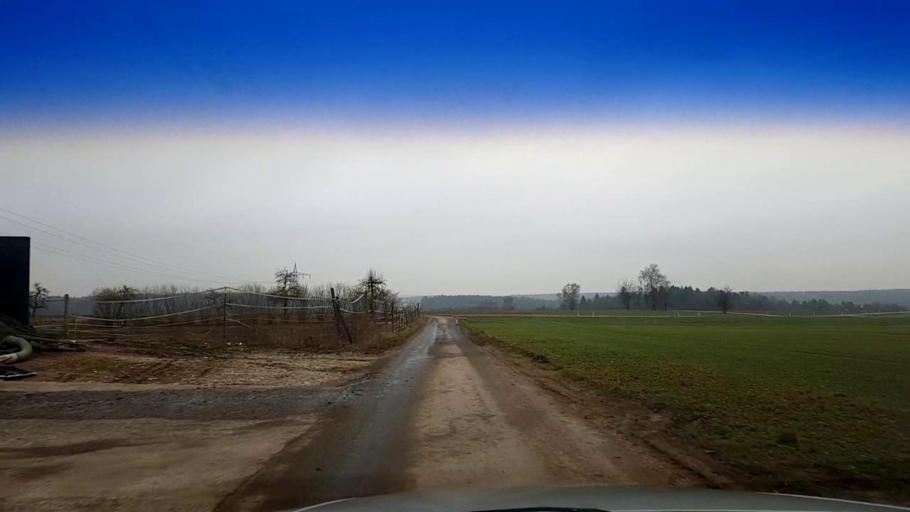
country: DE
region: Bavaria
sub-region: Upper Franconia
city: Zapfendorf
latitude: 49.9795
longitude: 10.9377
